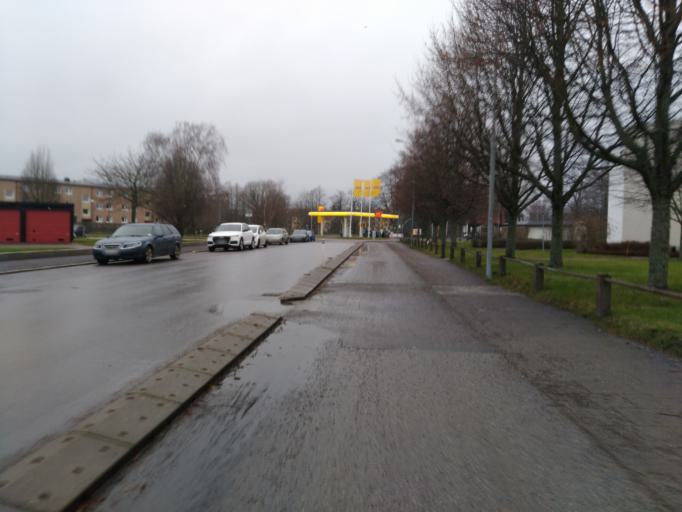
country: SE
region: Vaestra Goetaland
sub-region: Lidkopings Kommun
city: Lidkoping
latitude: 58.4944
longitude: 13.1554
